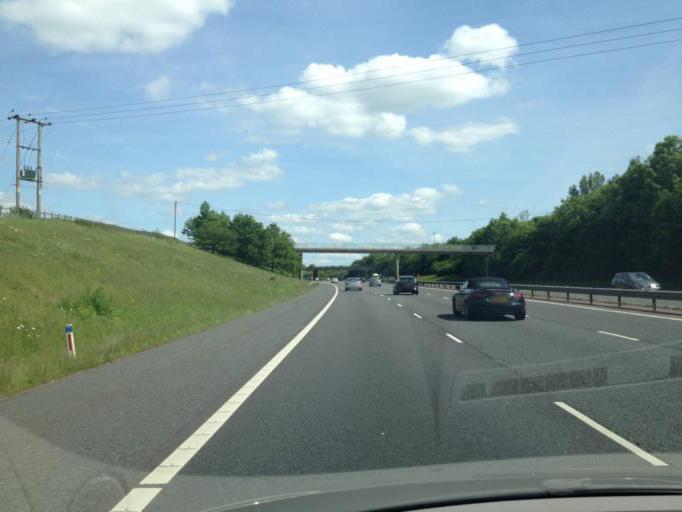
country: GB
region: England
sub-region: Oxfordshire
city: Wheatley
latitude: 51.7360
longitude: -1.0887
